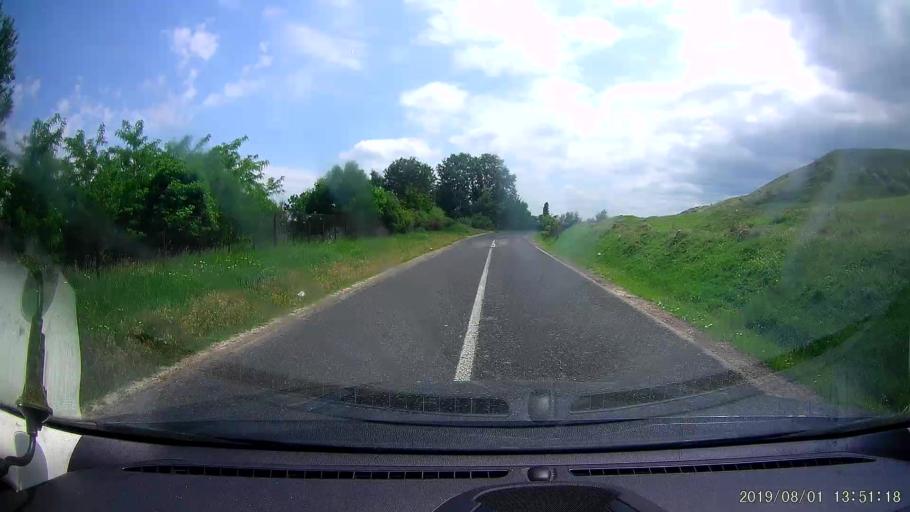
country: RO
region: Galati
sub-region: Comuna Vladesti
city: Vladesti
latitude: 45.8683
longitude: 28.0967
